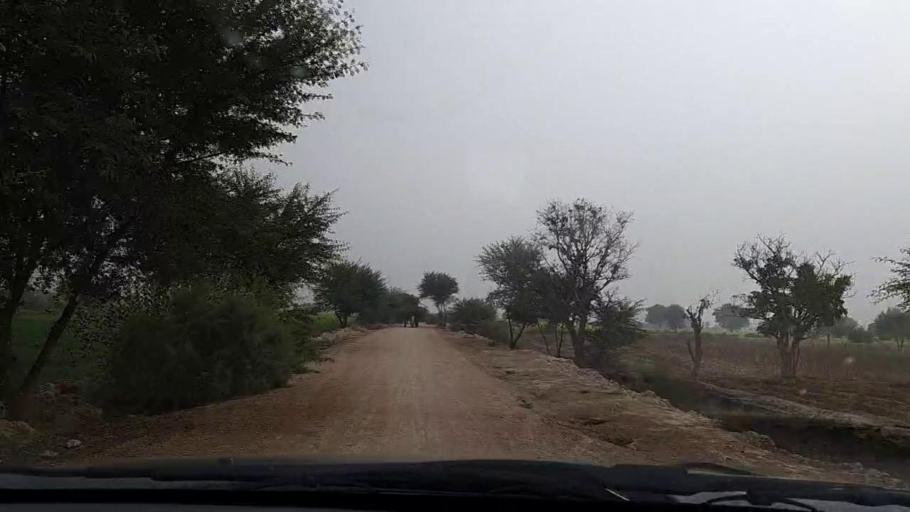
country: PK
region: Sindh
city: Pithoro
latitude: 25.7617
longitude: 69.3802
